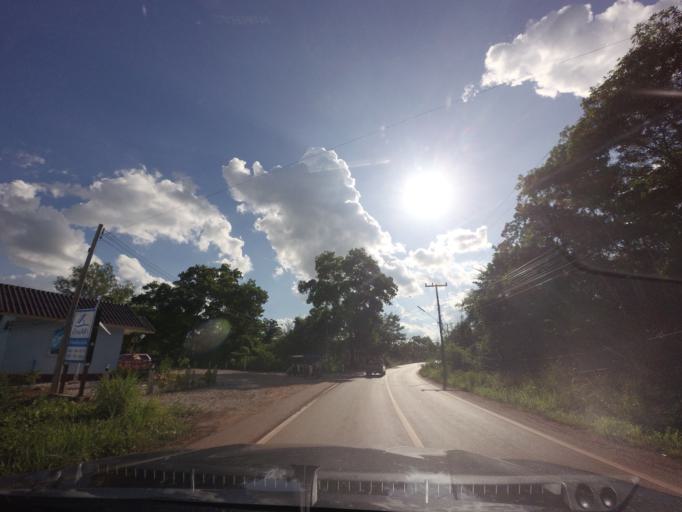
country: TH
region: Changwat Udon Thani
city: Ban Dung
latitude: 17.7452
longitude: 103.3238
